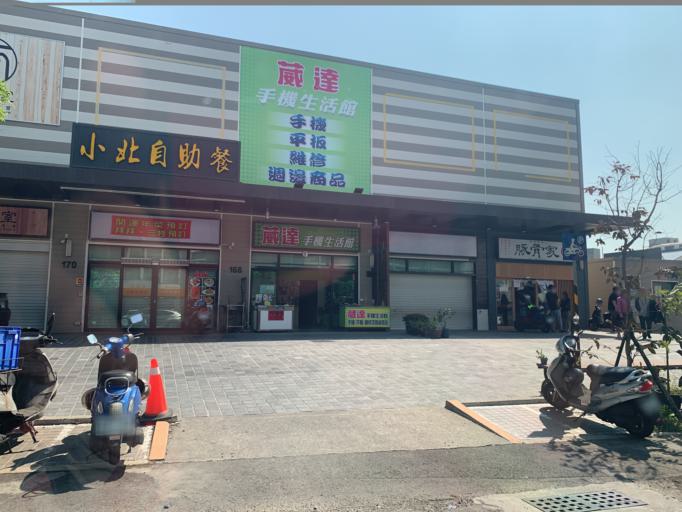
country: TW
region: Taiwan
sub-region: Tainan
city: Tainan
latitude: 23.0093
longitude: 120.2055
